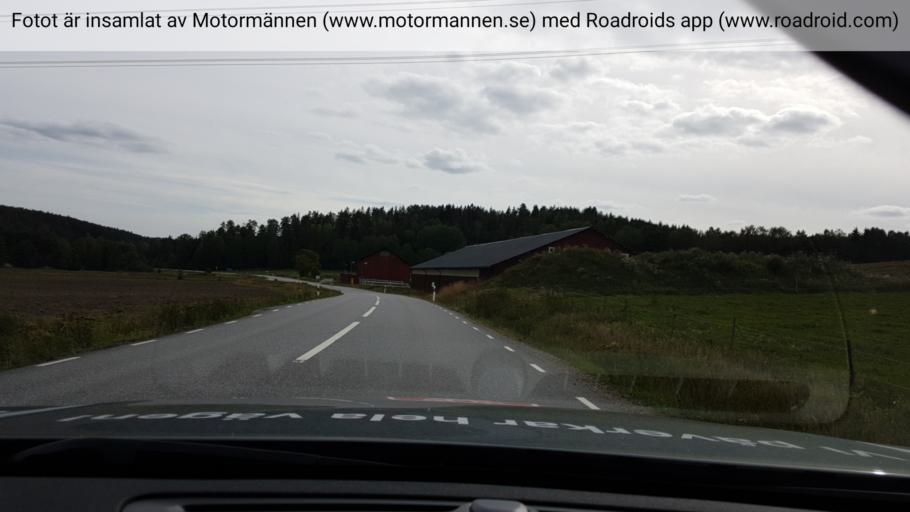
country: SE
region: Stockholm
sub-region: Botkyrka Kommun
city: Varsta
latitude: 59.1211
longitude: 17.8044
